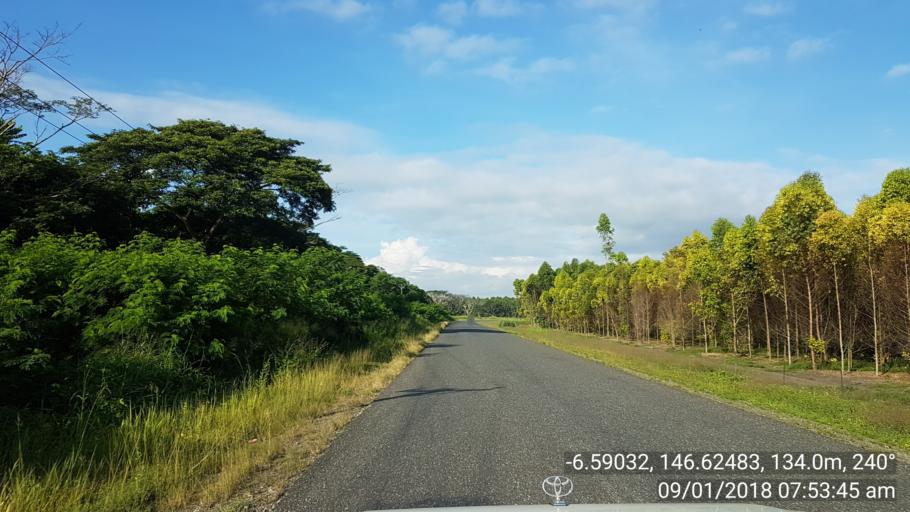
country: PG
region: Morobe
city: Lae
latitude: -6.5903
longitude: 146.6250
